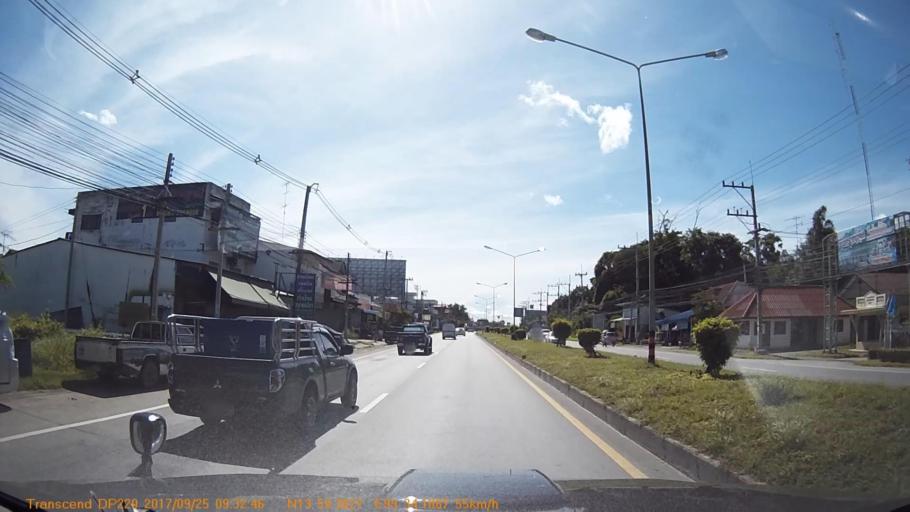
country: TH
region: Kanchanaburi
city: Kanchanaburi
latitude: 13.9896
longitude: 99.5687
